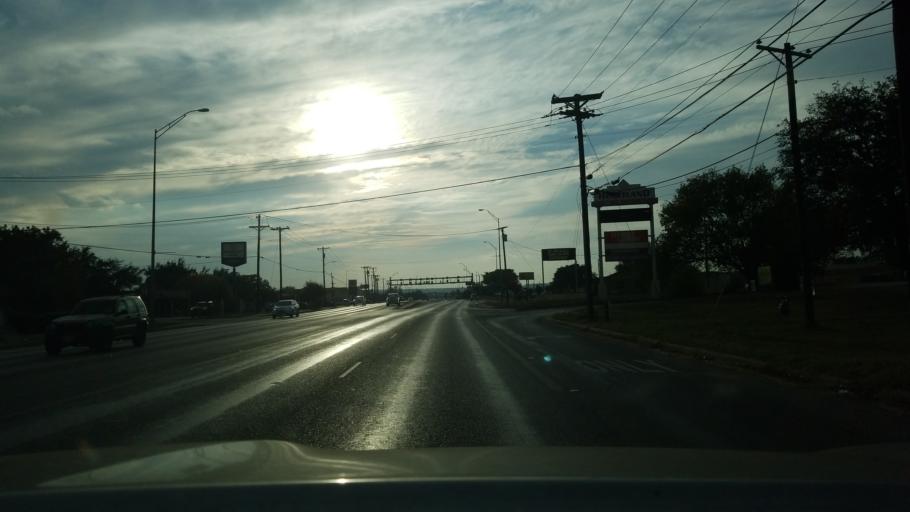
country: US
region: Texas
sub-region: Brown County
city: Early
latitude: 31.7363
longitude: -98.9605
